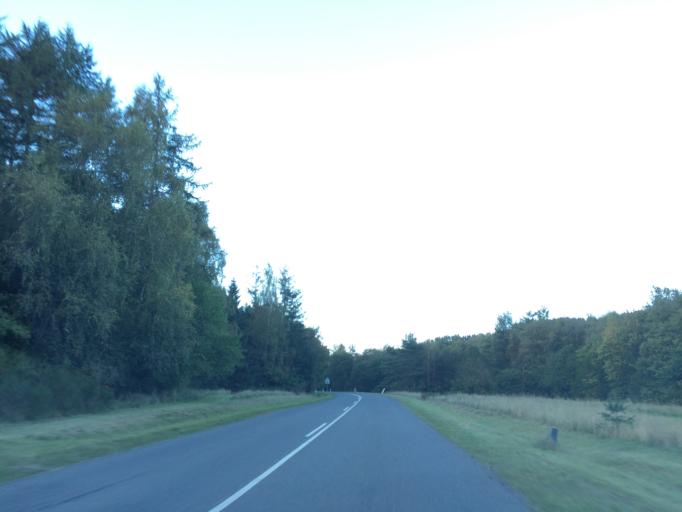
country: DK
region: Central Jutland
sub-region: Skanderborg Kommune
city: Ry
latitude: 56.0997
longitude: 9.7405
